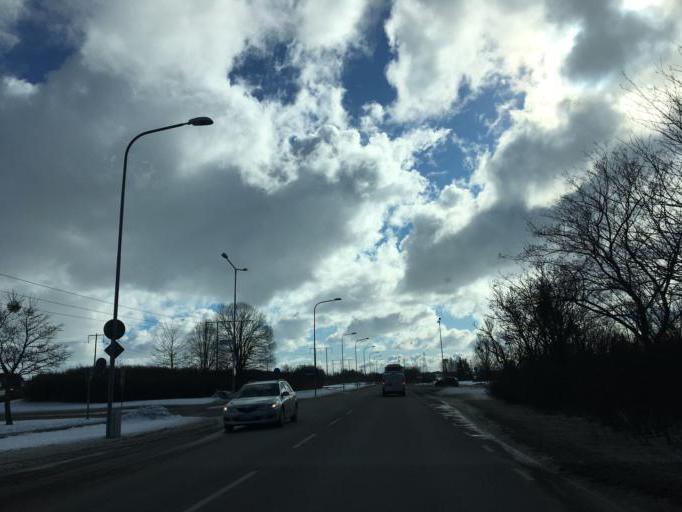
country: SE
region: Vaestmanland
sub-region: Vasteras
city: Vasteras
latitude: 59.5982
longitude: 16.4631
